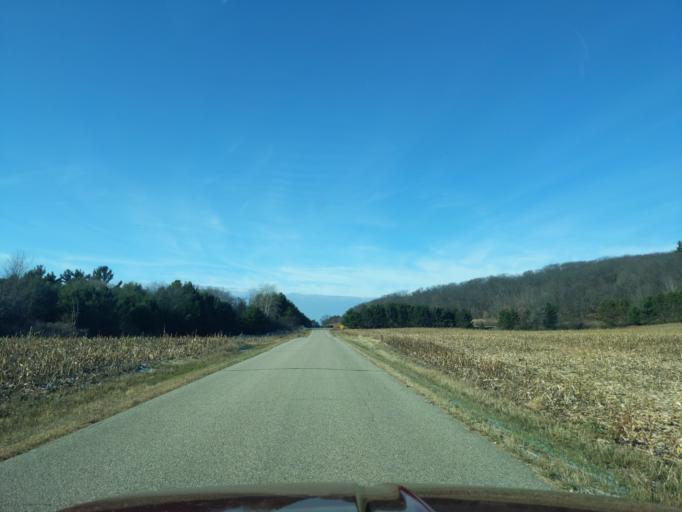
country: US
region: Wisconsin
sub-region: Waushara County
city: Silver Lake
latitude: 44.1131
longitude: -89.1758
